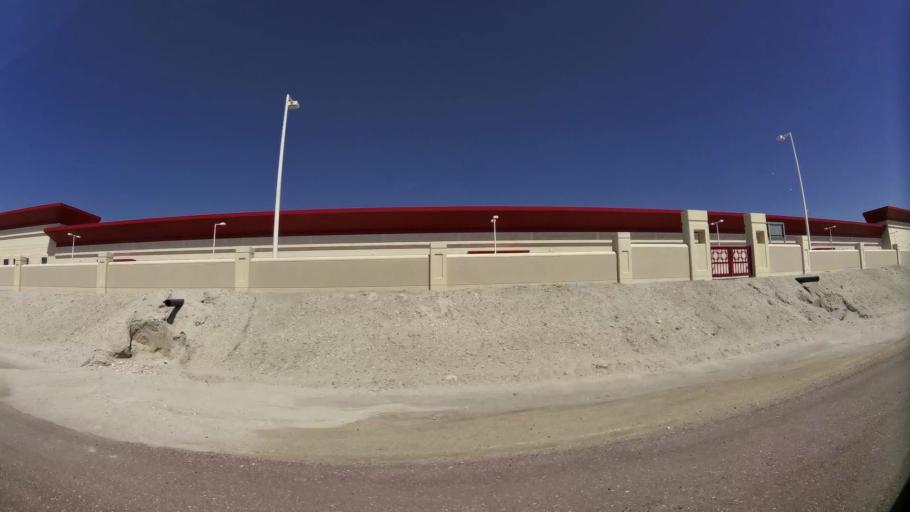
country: BH
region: Muharraq
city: Al Muharraq
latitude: 26.3056
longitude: 50.6231
